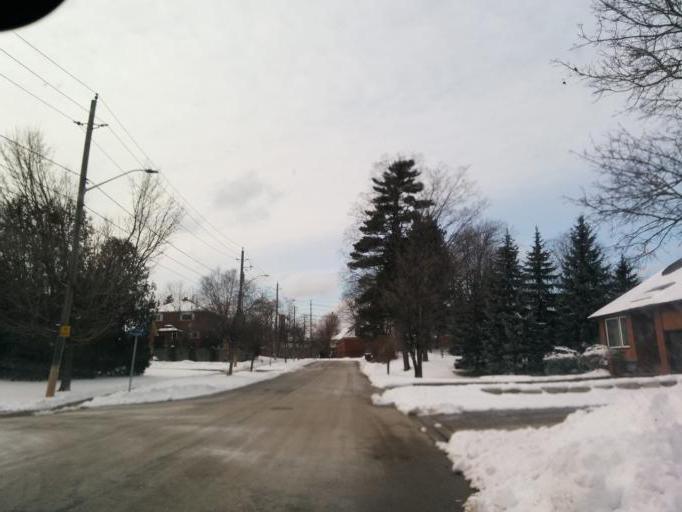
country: CA
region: Ontario
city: Mississauga
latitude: 43.5372
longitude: -79.6625
